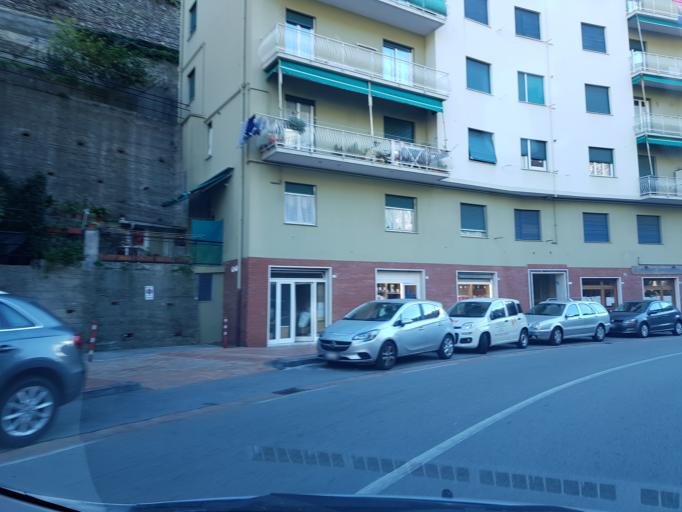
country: IT
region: Liguria
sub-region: Provincia di Genova
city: Bogliasco
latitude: 44.3865
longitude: 9.0344
